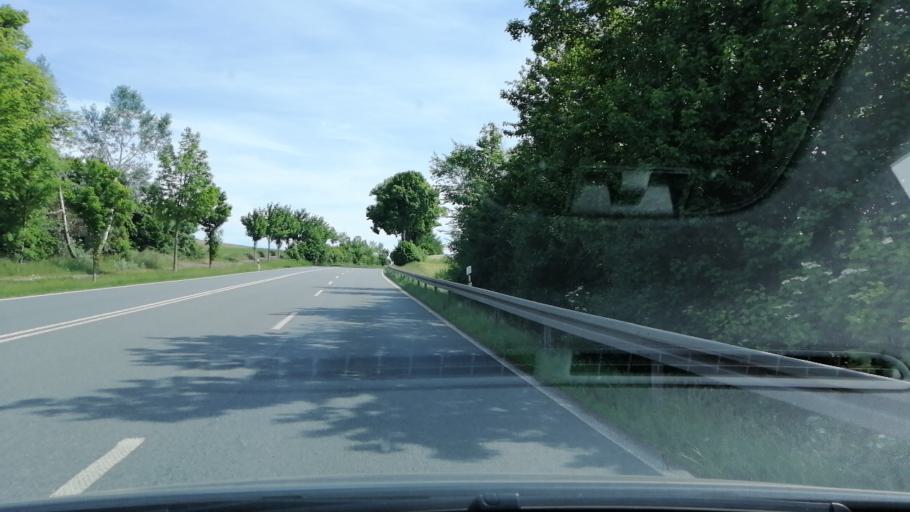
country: DE
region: Hesse
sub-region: Regierungsbezirk Kassel
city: Bad Wildungen
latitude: 51.1463
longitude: 9.1173
